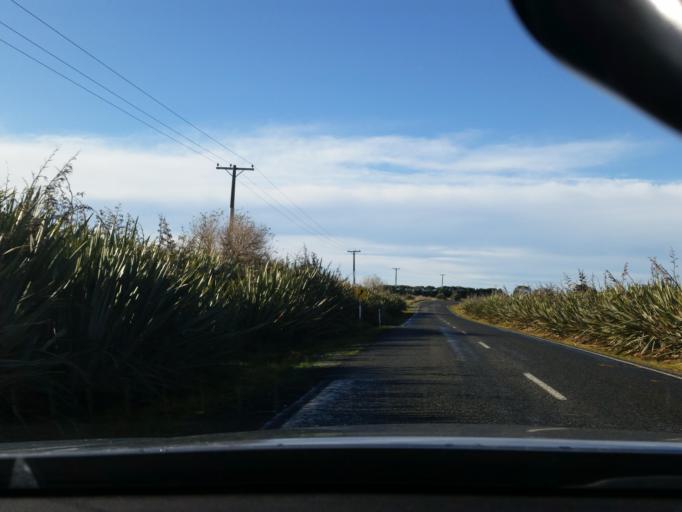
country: NZ
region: Southland
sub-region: Southland District
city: Riverton
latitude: -46.1454
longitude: 168.0230
